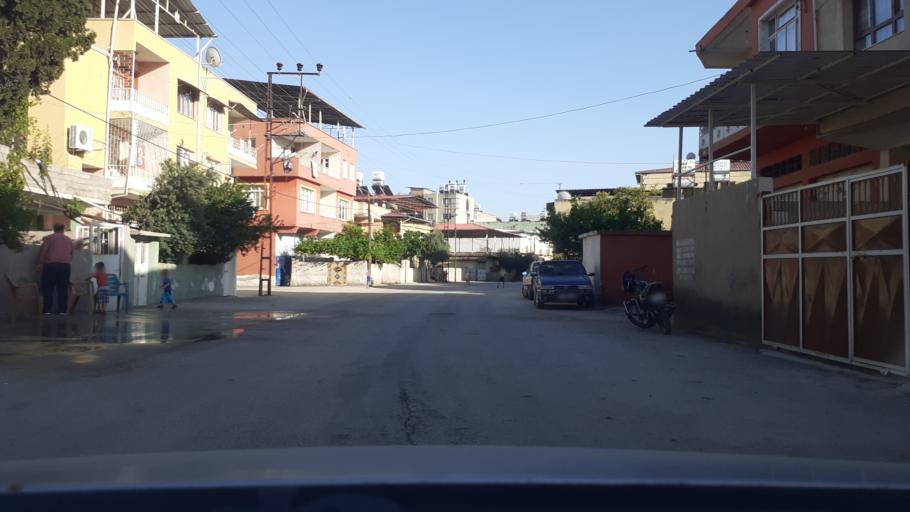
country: TR
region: Hatay
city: Kirikhan
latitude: 36.5008
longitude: 36.3648
